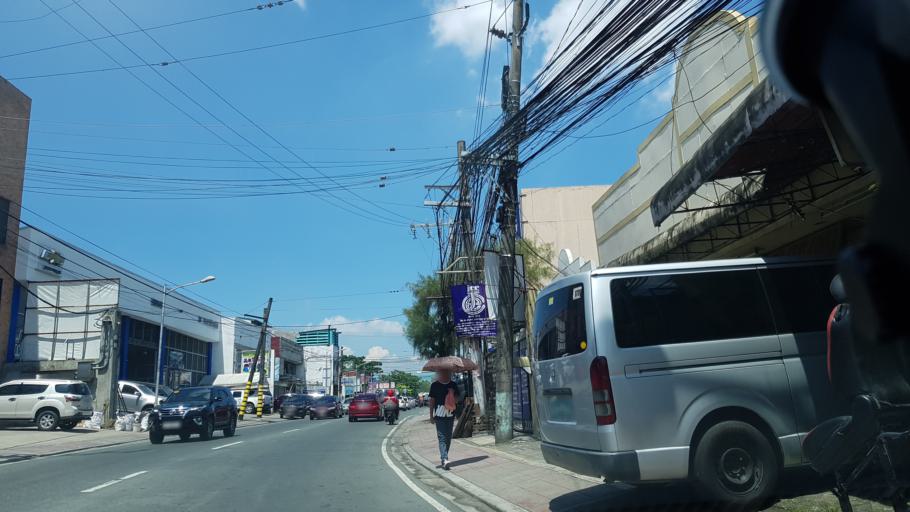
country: PH
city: Sambayanihan People's Village
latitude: 14.4530
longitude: 121.0300
